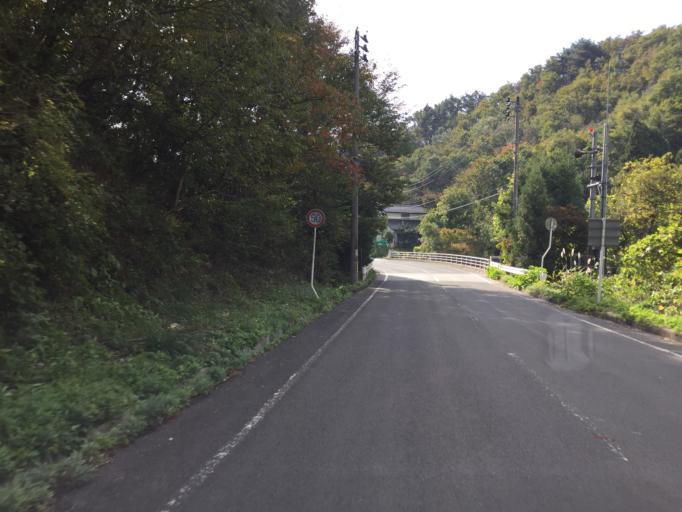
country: JP
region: Fukushima
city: Fukushima-shi
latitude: 37.7977
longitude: 140.3884
